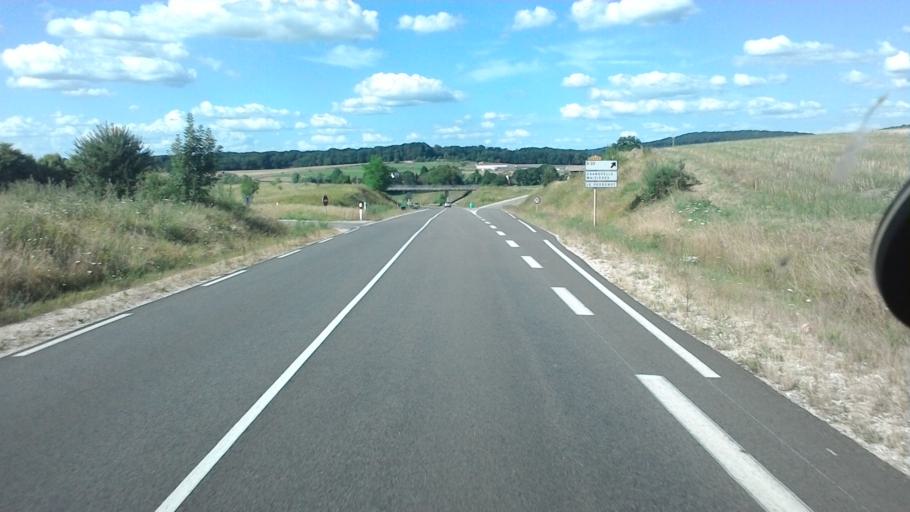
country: FR
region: Franche-Comte
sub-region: Departement de la Haute-Saone
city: Rioz
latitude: 47.5025
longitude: 5.9855
